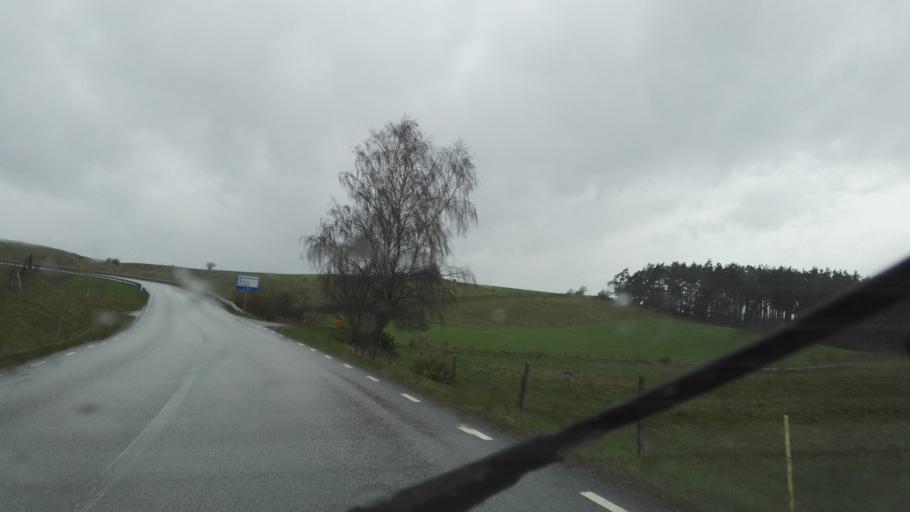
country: SE
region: Skane
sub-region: Kristianstads Kommun
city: Degeberga
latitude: 55.7212
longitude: 14.1282
